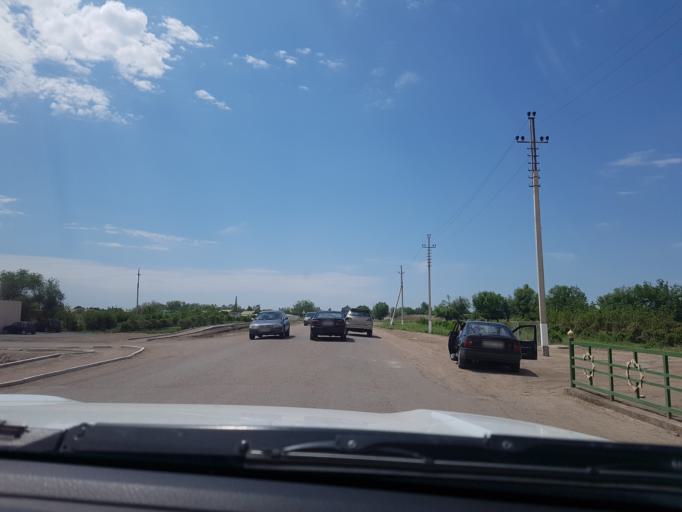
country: TM
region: Dasoguz
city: Koeneuergench
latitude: 42.3229
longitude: 59.1402
